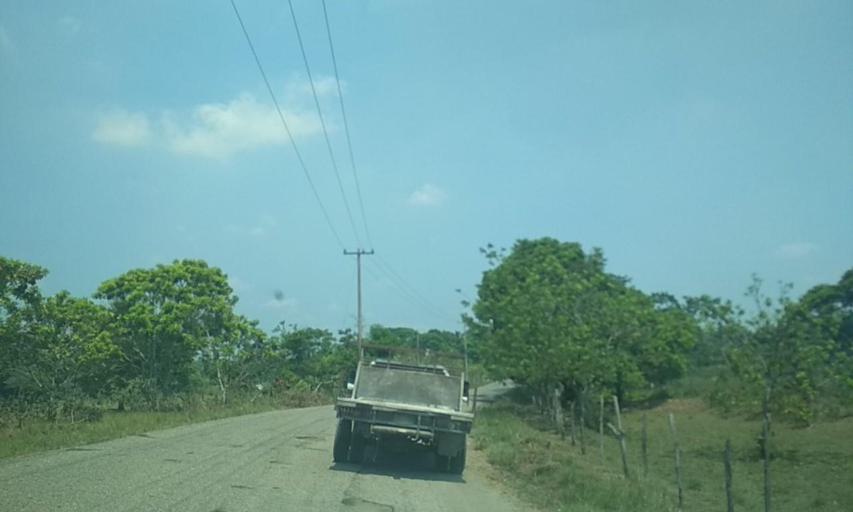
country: MX
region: Tabasco
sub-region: Huimanguillo
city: C-41 (Licenciado Carlos A. Madrazo)
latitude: 17.8309
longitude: -93.5081
